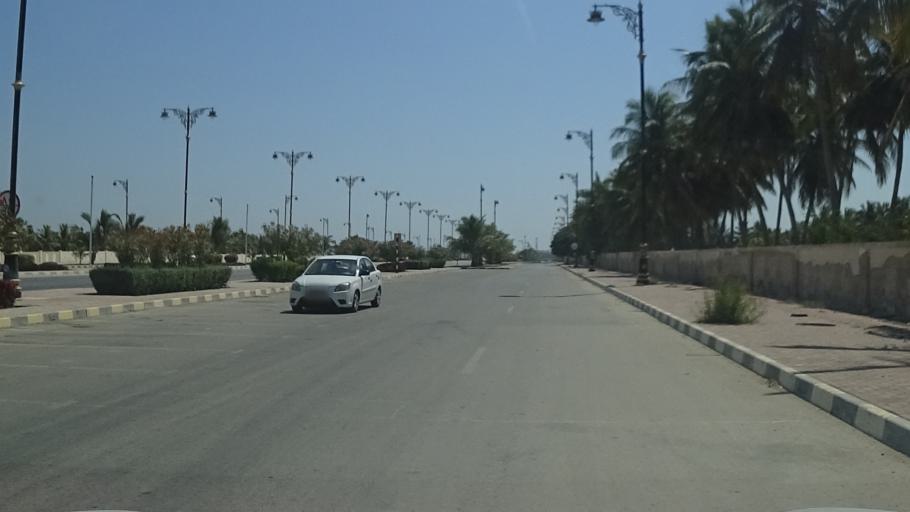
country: OM
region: Zufar
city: Salalah
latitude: 17.0337
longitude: 54.1719
